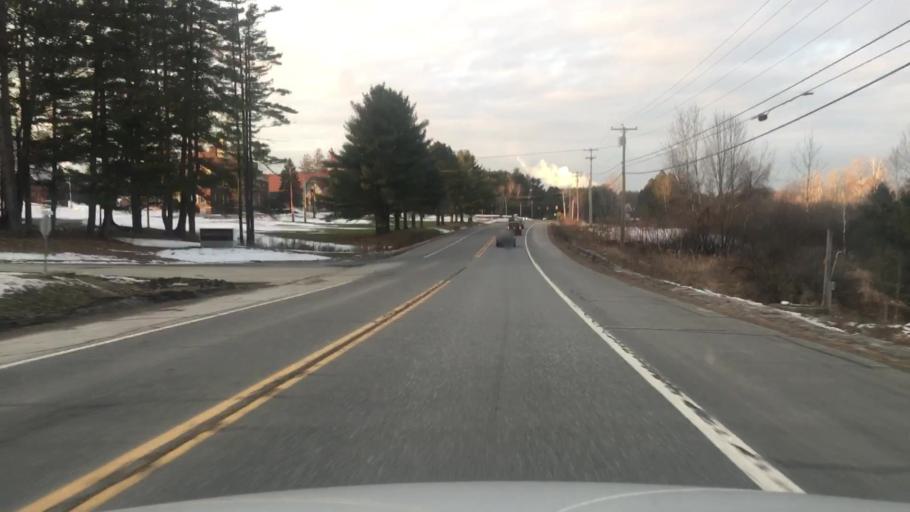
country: US
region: Maine
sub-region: Somerset County
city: Fairfield
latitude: 44.6669
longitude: -69.6287
